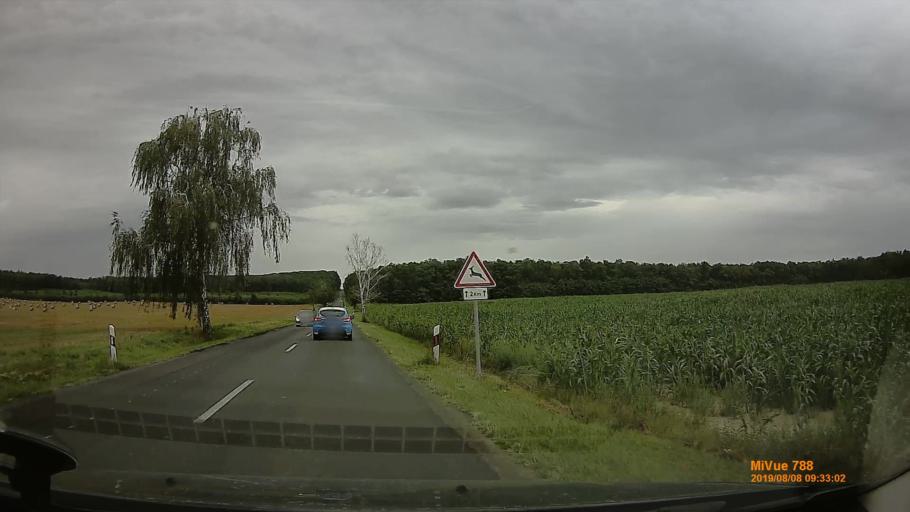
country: HU
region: Vas
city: Vasvar
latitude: 47.0176
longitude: 16.8222
